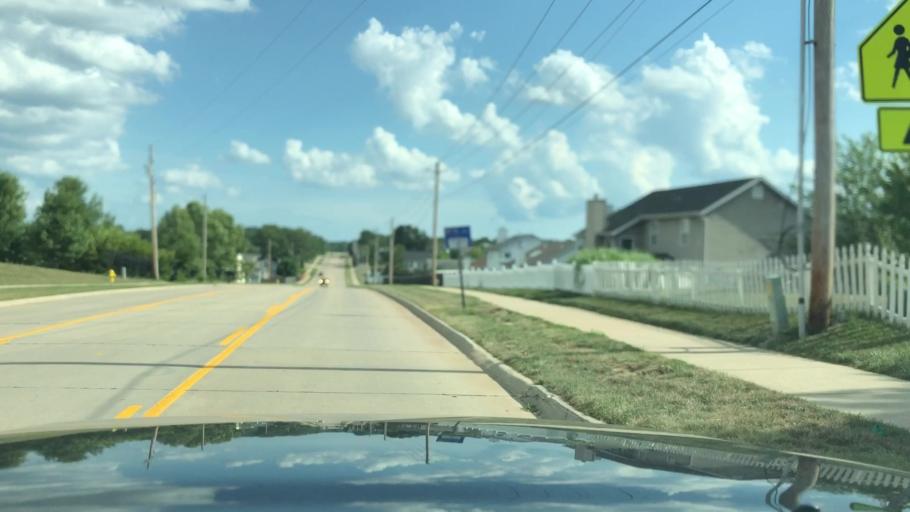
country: US
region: Missouri
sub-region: Saint Charles County
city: Wentzville
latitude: 38.8360
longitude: -90.8922
